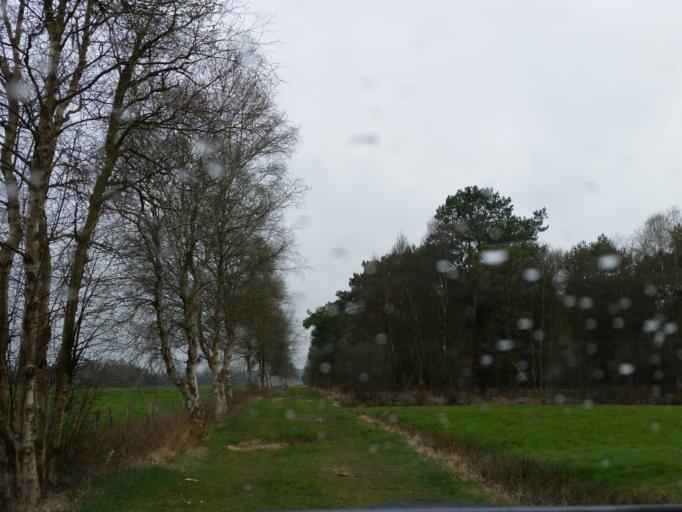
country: DE
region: Lower Saxony
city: Stinstedt
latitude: 53.6022
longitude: 8.9829
